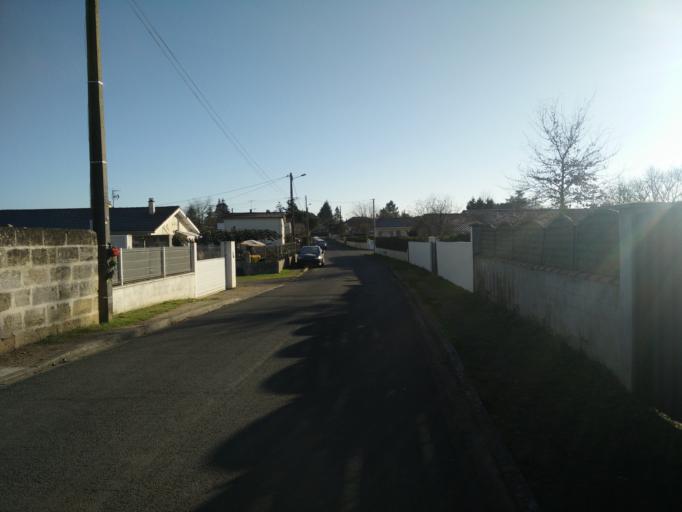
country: FR
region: Aquitaine
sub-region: Departement de la Gironde
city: Libourne
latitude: 44.9531
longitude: -0.2345
